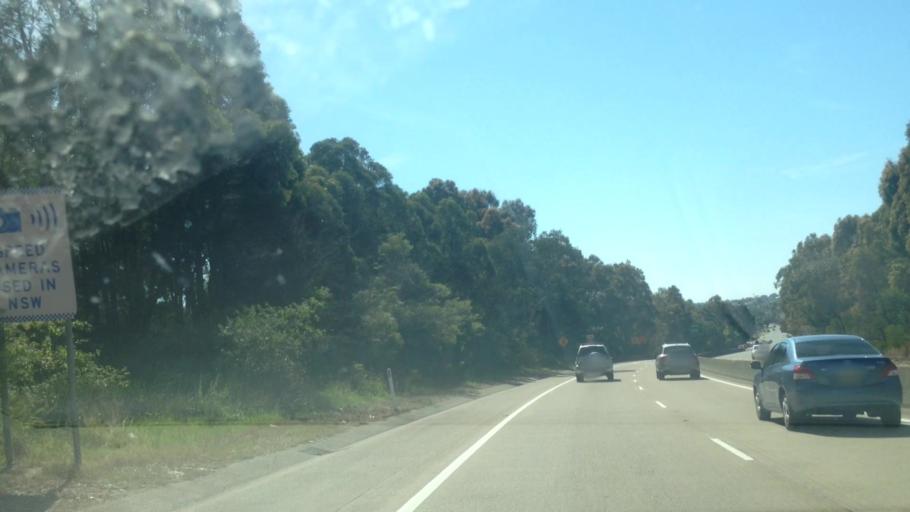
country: AU
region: New South Wales
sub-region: Newcastle
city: Elermore Vale
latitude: -32.9085
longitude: 151.6589
